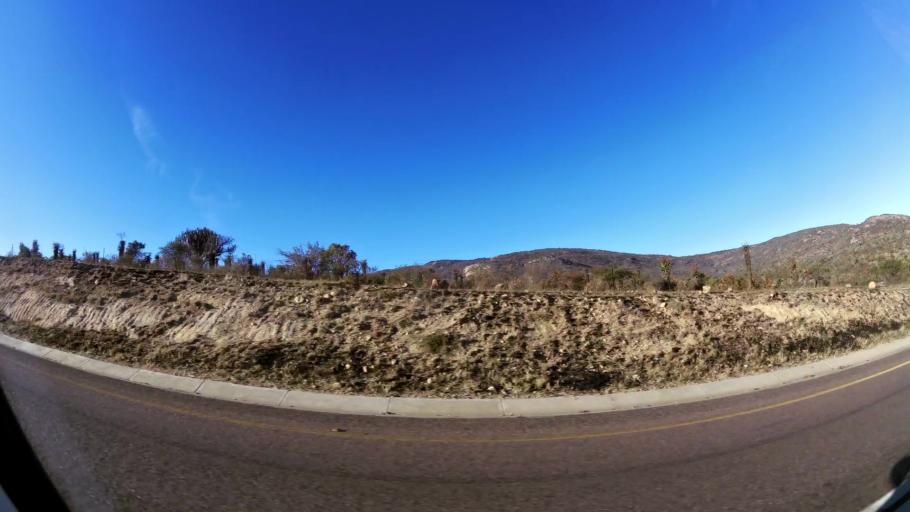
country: ZA
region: Limpopo
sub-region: Capricorn District Municipality
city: Mankoeng
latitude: -23.9313
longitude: 29.8498
